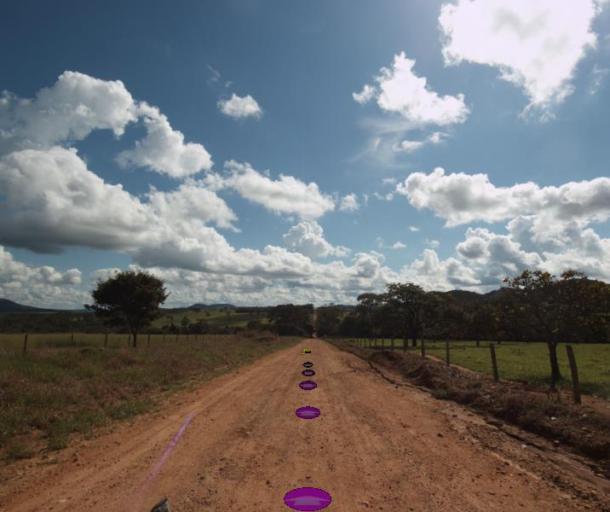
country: BR
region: Goias
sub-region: Pirenopolis
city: Pirenopolis
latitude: -15.8289
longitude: -49.1399
